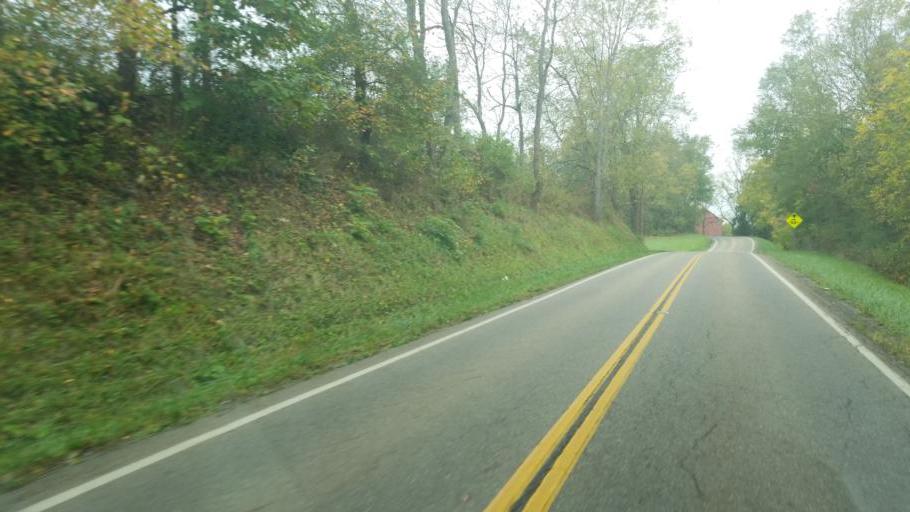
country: US
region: Ohio
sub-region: Carroll County
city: Lake Mohawk
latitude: 40.6165
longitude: -81.2772
